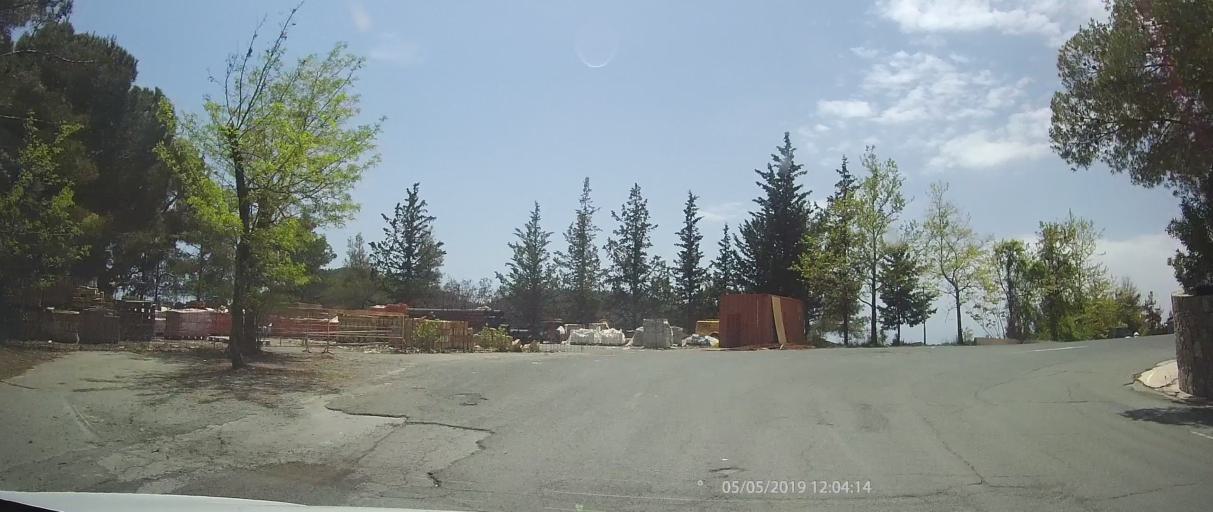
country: CY
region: Lefkosia
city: Kakopetria
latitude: 34.9829
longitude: 32.7391
